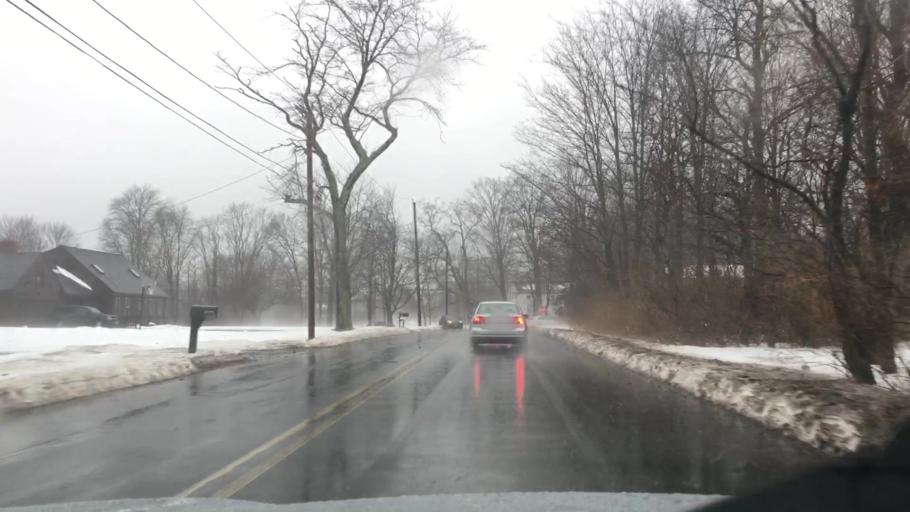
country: US
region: Massachusetts
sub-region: Hampshire County
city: Granby
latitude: 42.2250
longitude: -72.4970
